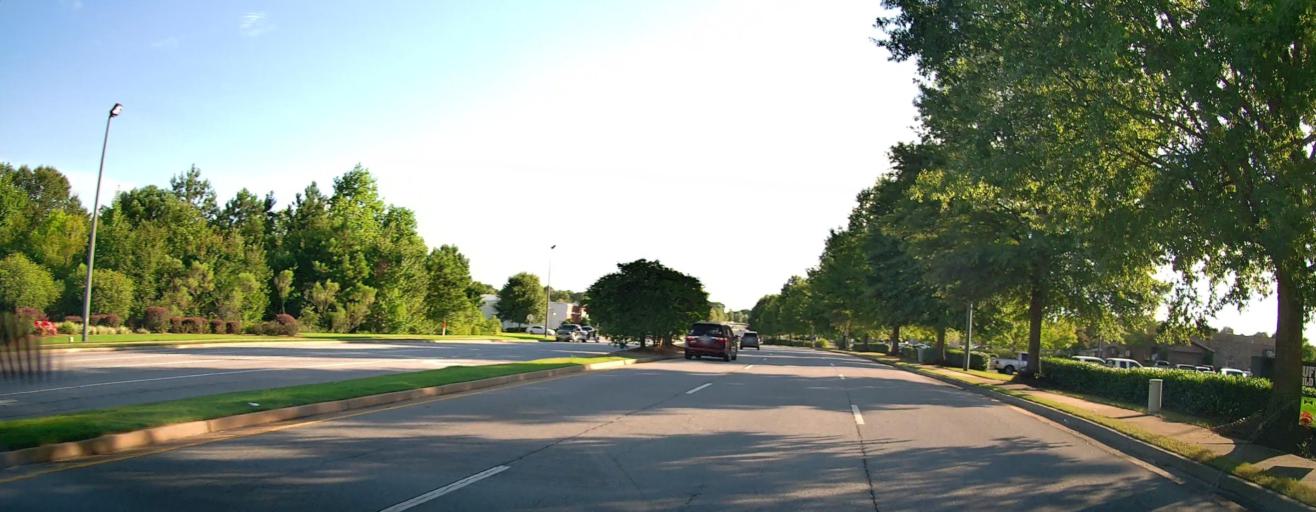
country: US
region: Alabama
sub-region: Russell County
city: Phenix City
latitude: 32.5455
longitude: -84.9462
